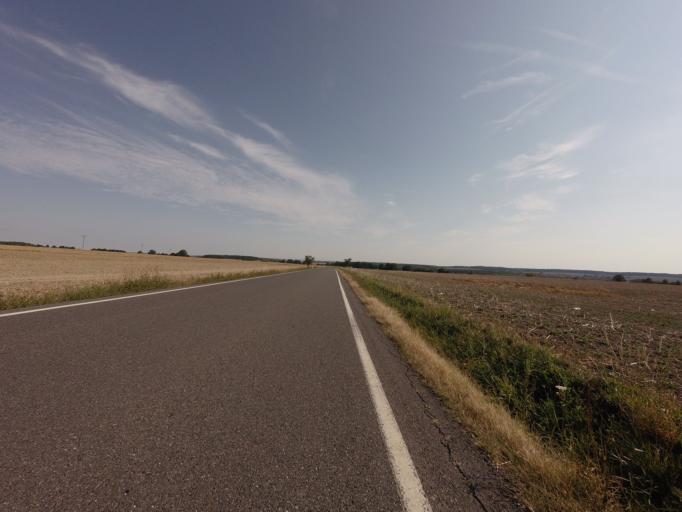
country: CZ
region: Jihocesky
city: Bernartice
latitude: 49.3348
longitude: 14.3625
